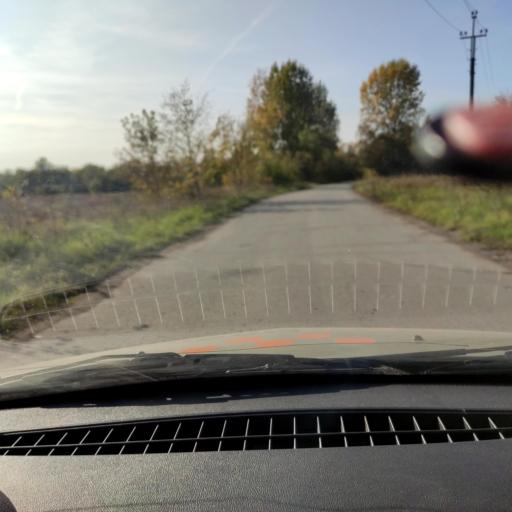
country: RU
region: Bashkortostan
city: Iglino
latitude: 54.7977
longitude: 56.2155
